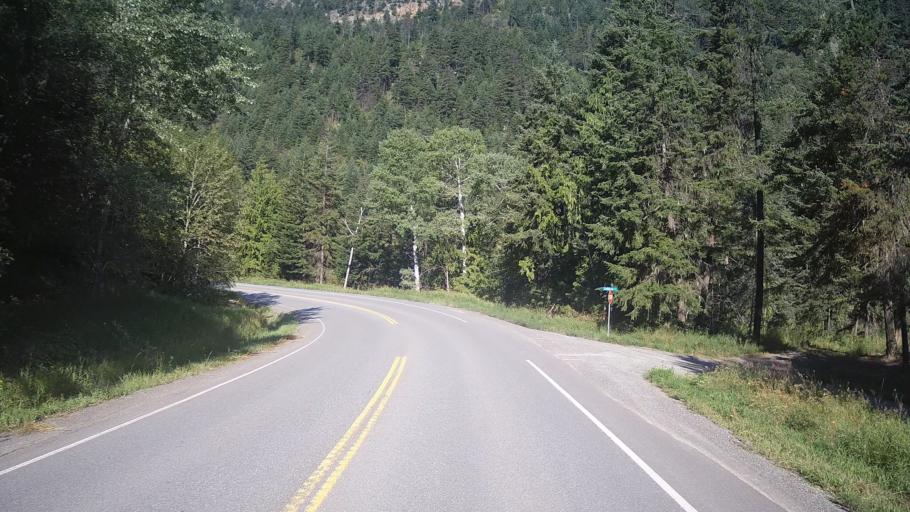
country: CA
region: British Columbia
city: Lillooet
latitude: 50.6388
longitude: -122.0867
